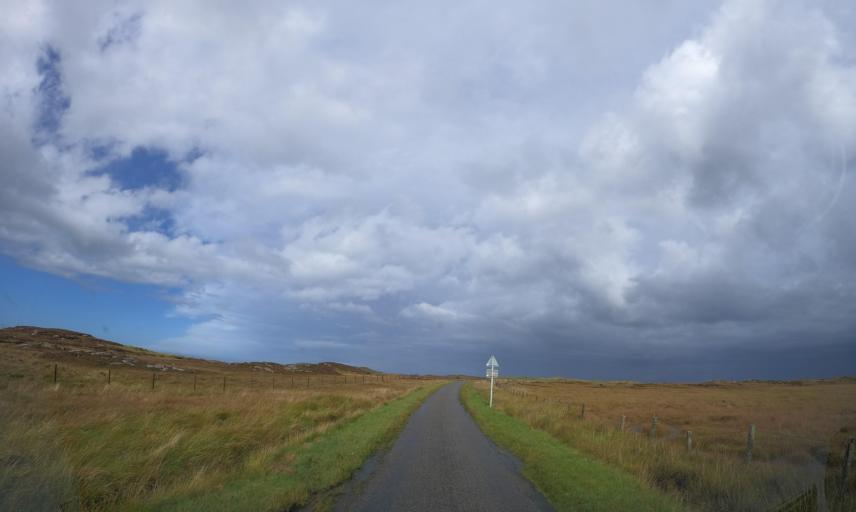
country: GB
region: Scotland
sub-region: Eilean Siar
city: Barra
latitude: 56.5186
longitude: -6.8381
